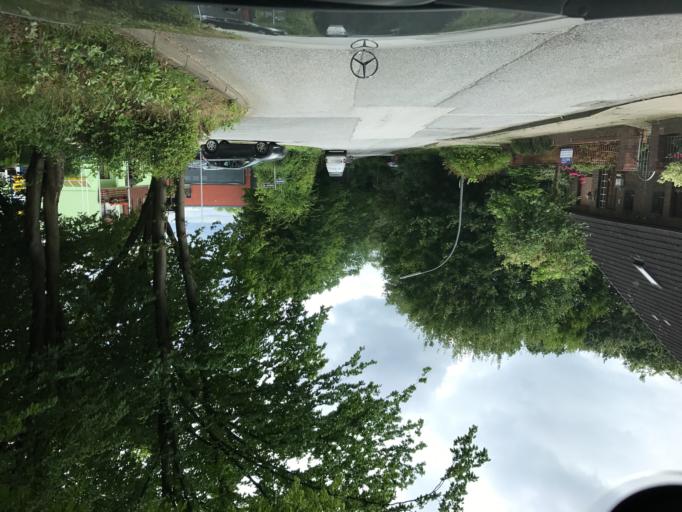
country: DE
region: Schleswig-Holstein
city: Glinde
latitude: 53.5132
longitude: 10.2094
